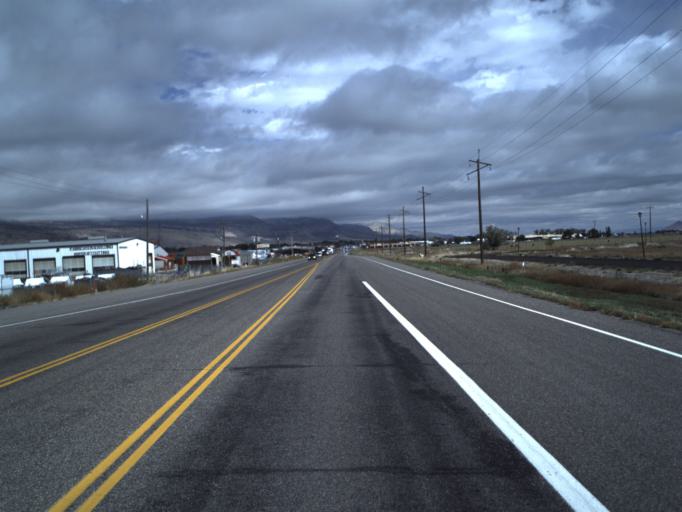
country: US
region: Utah
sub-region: Sevier County
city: Richfield
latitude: 38.7359
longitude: -112.0945
